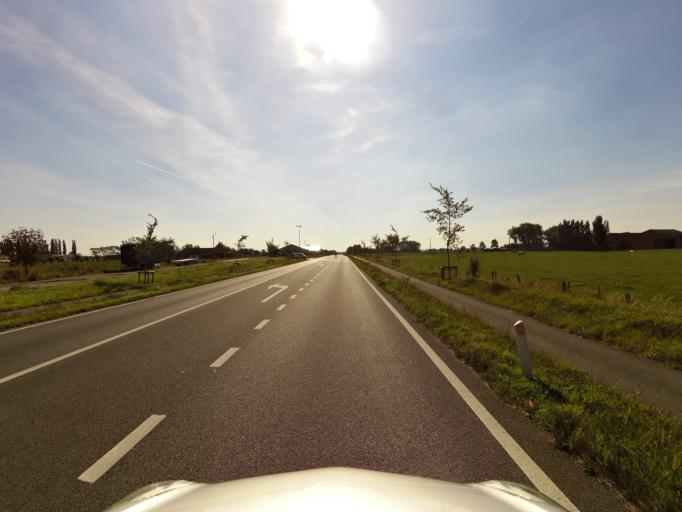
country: BE
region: Flanders
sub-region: Provincie West-Vlaanderen
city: Diksmuide
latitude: 51.1112
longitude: 2.8908
